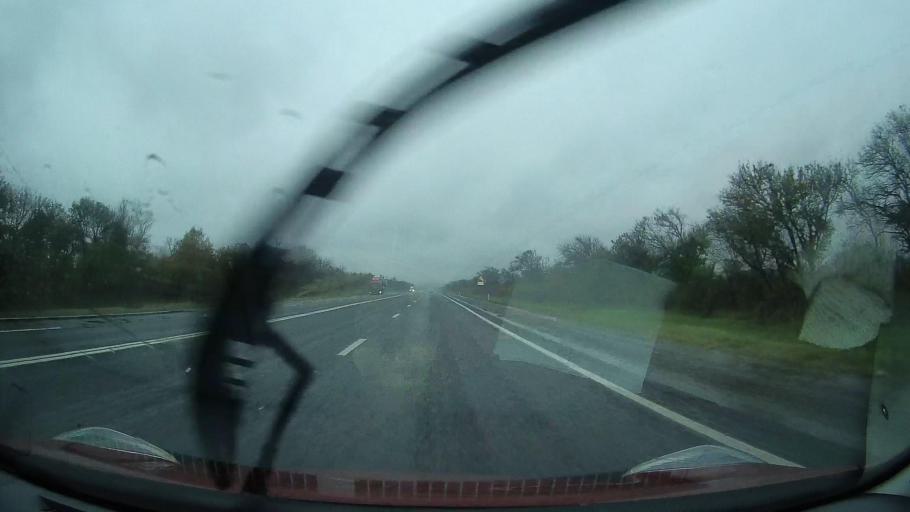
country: RU
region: Stavropol'skiy
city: Nevinnomyssk
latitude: 44.6167
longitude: 42.1034
